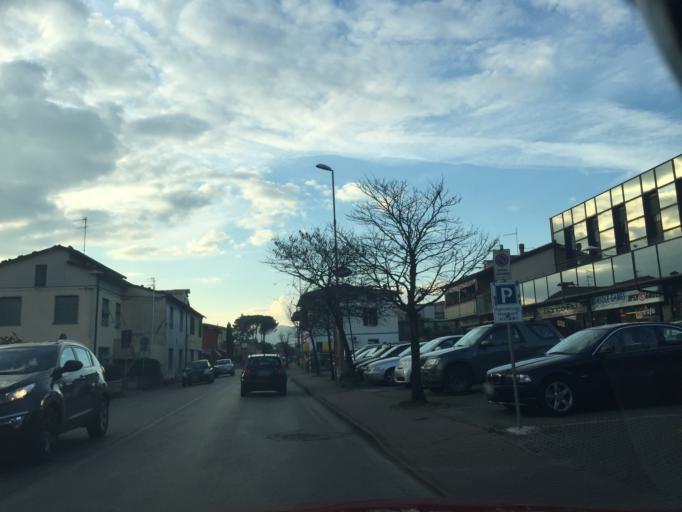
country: IT
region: Tuscany
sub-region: Provincia di Pistoia
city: Monsummano Terme
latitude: 43.8720
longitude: 10.8096
